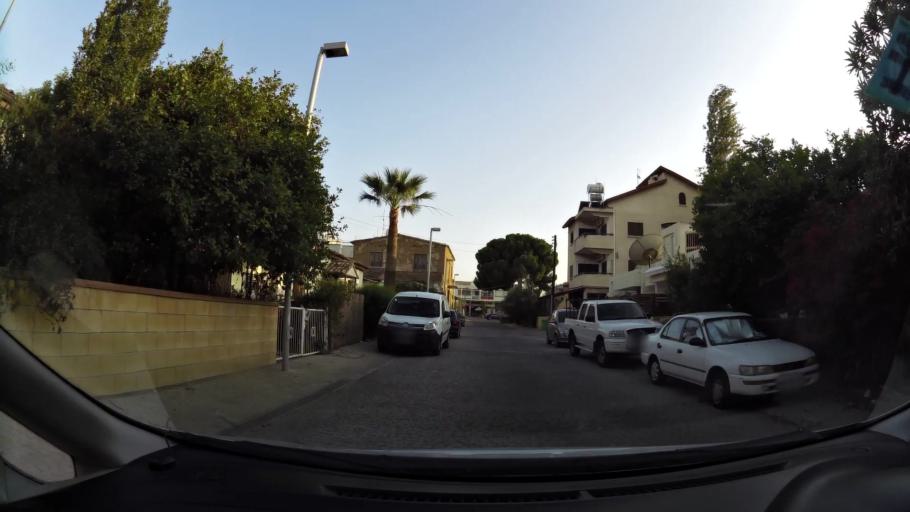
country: CY
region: Lefkosia
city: Nicosia
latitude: 35.1693
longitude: 33.3322
